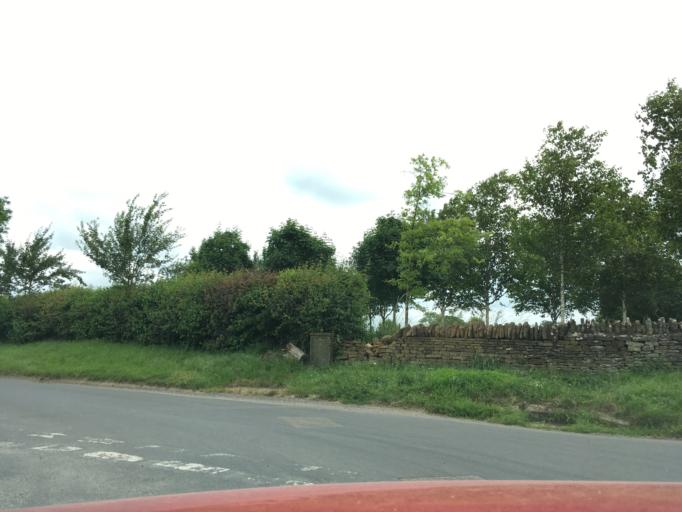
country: GB
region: England
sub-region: Oxfordshire
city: Bloxham
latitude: 51.9514
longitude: -1.3928
